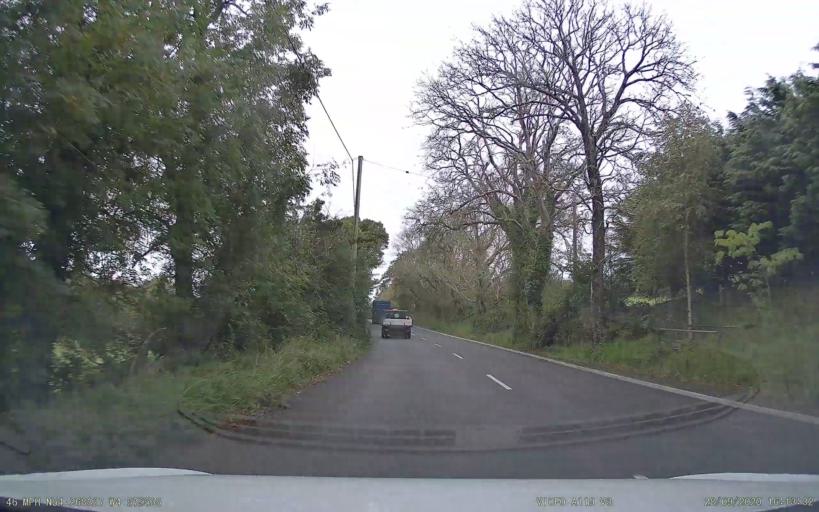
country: IM
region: Douglas
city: Douglas
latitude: 54.2683
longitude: -4.5795
